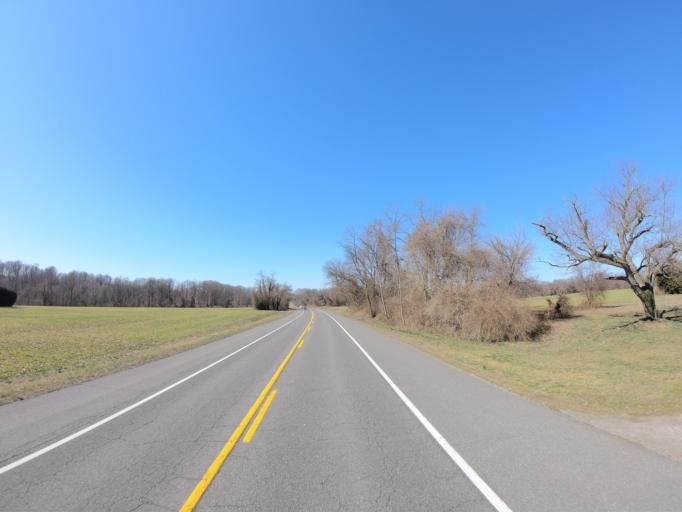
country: US
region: Delaware
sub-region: New Castle County
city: Townsend
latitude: 39.3436
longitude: -75.8611
